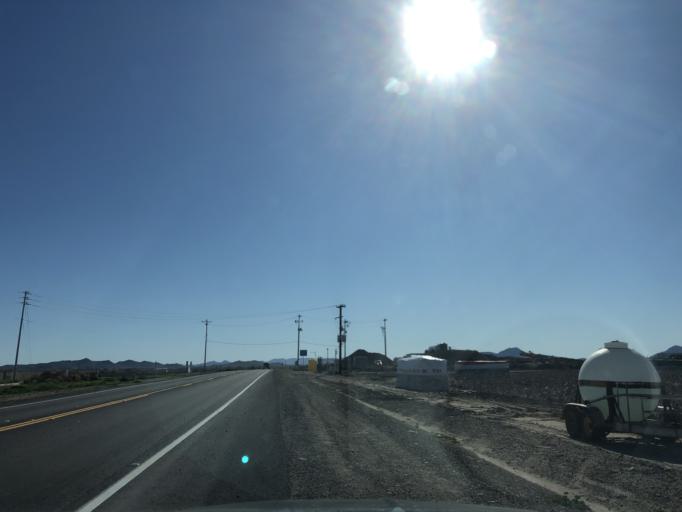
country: US
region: Arizona
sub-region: Maricopa County
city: Buckeye
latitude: 33.3751
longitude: -112.4779
